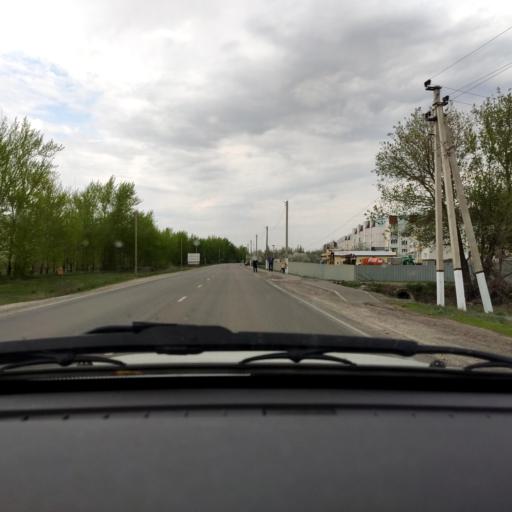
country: RU
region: Voronezj
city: Novaya Usman'
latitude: 51.6045
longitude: 39.3734
